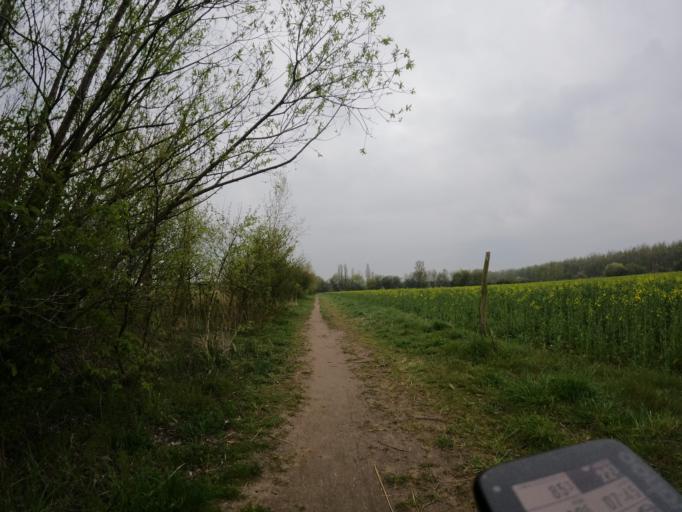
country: DE
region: Berlin
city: Lichtenrade
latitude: 52.3910
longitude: 13.4302
